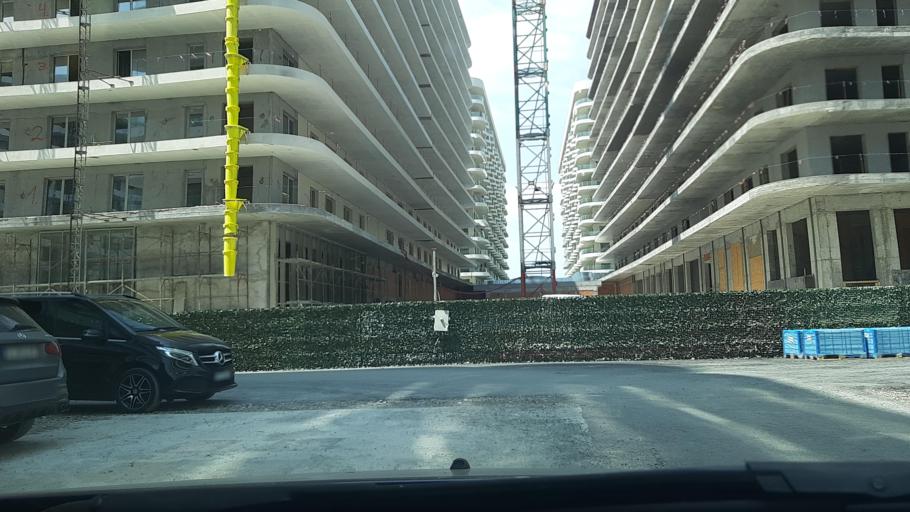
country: RO
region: Constanta
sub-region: Comuna Navodari
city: Navodari
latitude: 44.2767
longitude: 28.6205
